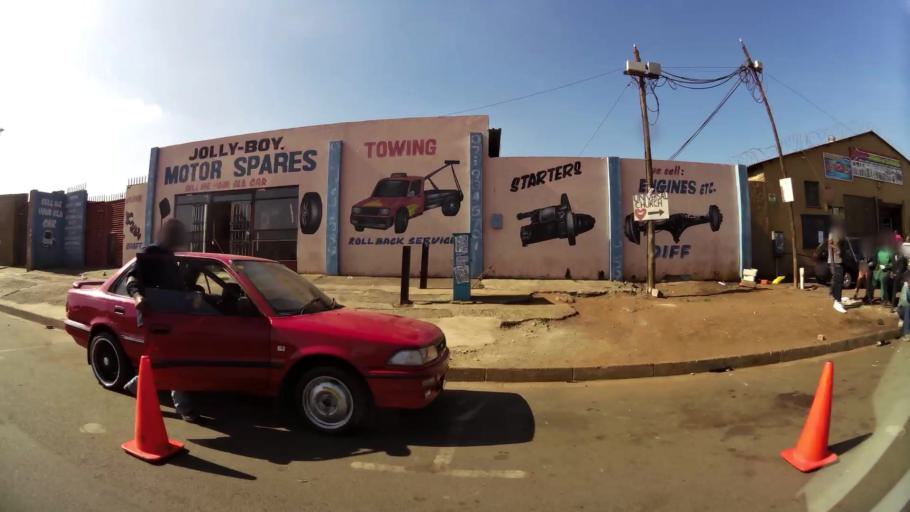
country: ZA
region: Gauteng
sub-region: City of Johannesburg Metropolitan Municipality
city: Soweto
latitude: -26.2888
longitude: 27.8499
